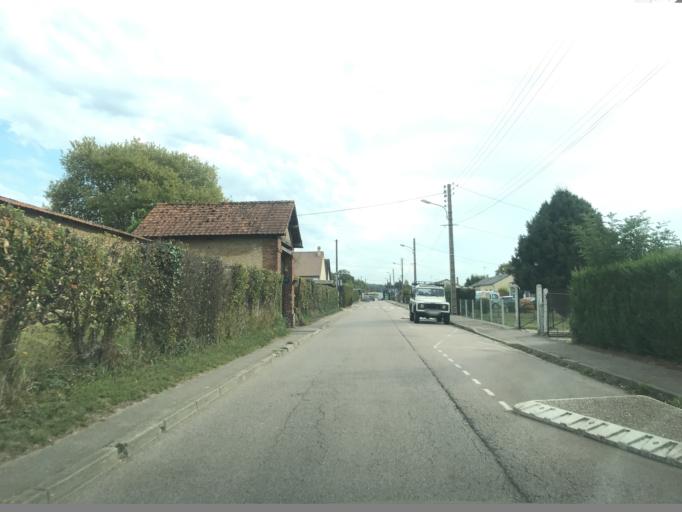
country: FR
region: Haute-Normandie
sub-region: Departement de l'Eure
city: Louviers
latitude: 49.2057
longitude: 1.1850
